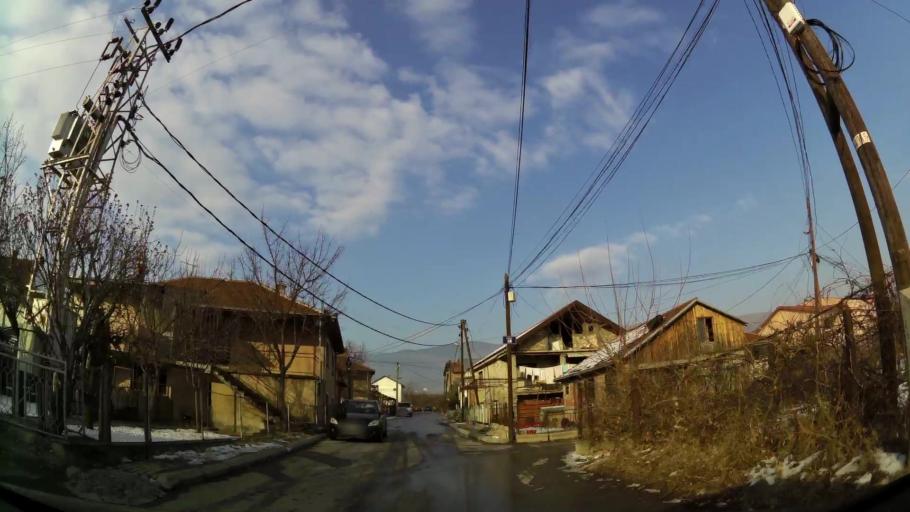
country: MK
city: Creshevo
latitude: 42.0324
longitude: 21.5178
